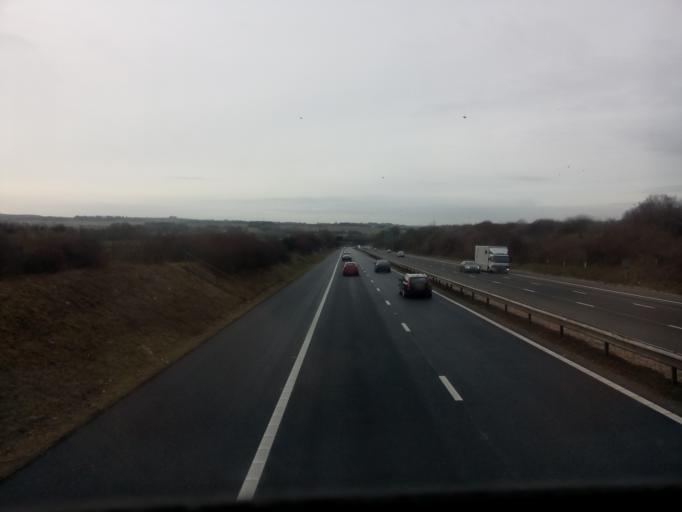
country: GB
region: England
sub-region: Hampshire
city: Kings Worthy
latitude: 51.1006
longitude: -1.2732
